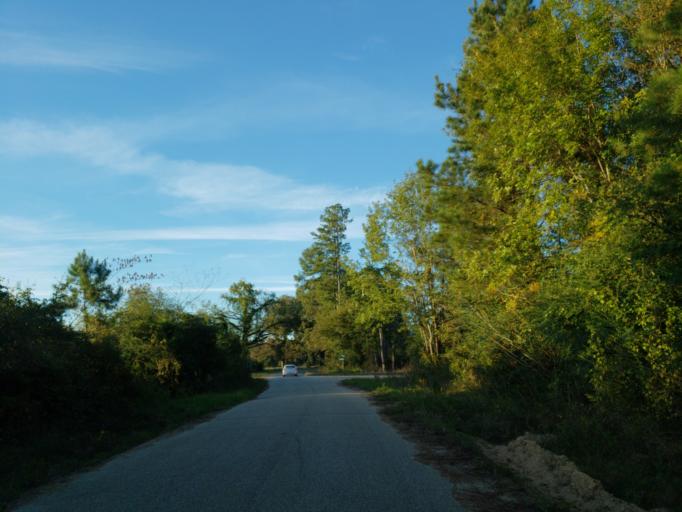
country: US
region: Mississippi
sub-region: Wayne County
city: Belmont
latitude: 31.4353
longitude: -88.5262
